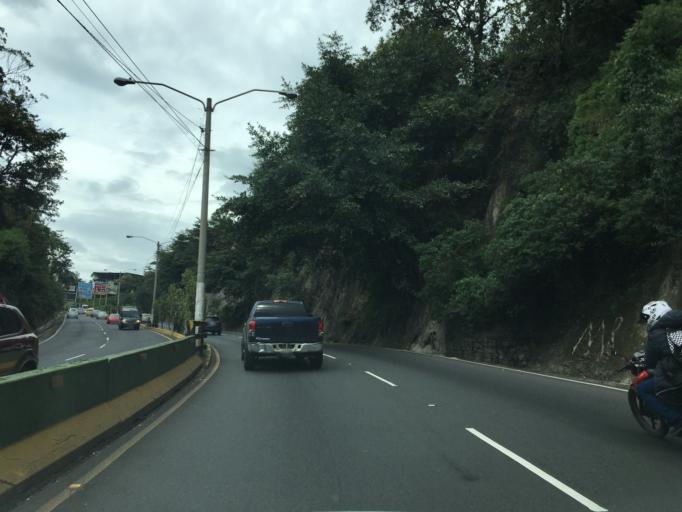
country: GT
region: Guatemala
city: Mixco
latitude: 14.5930
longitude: -90.5715
